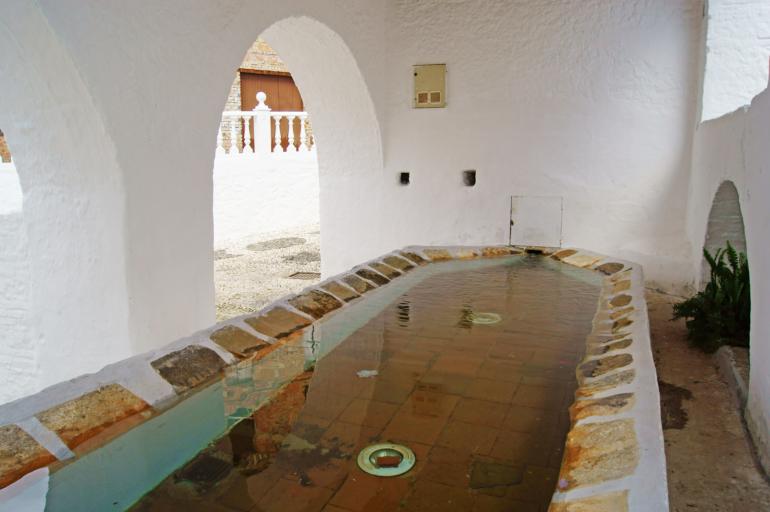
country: ES
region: Andalusia
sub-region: Provincia de Malaga
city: Monda
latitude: 36.6296
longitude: -4.8310
